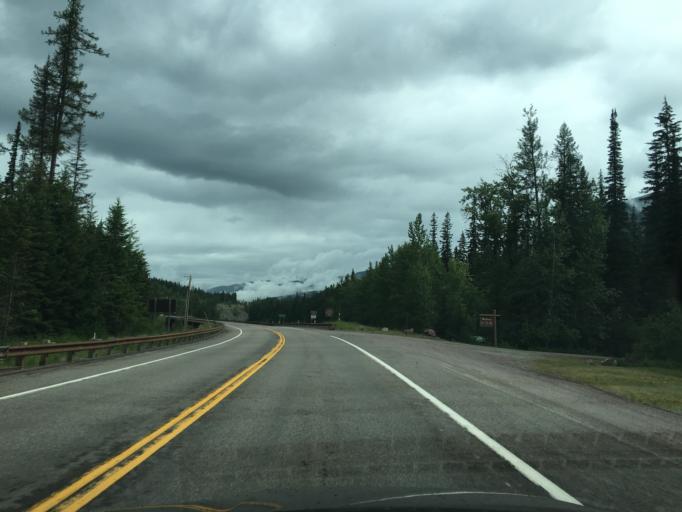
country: US
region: Montana
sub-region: Flathead County
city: Bigfork
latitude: 48.2729
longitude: -113.6038
